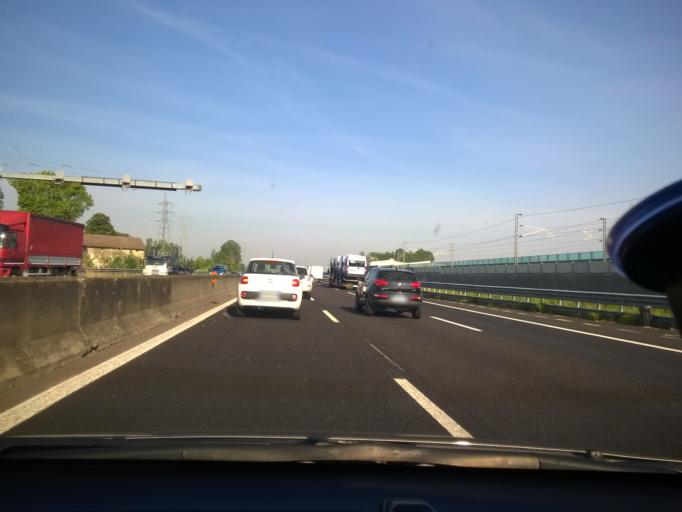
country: IT
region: Emilia-Romagna
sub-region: Provincia di Reggio Emilia
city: Reggio nell'Emilia
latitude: 44.7322
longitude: 10.6162
